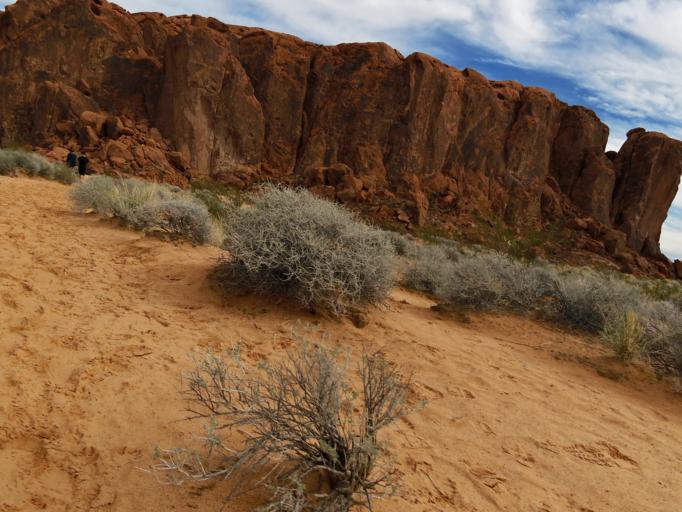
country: US
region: Nevada
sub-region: Clark County
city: Moapa Valley
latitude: 36.4887
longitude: -114.5274
